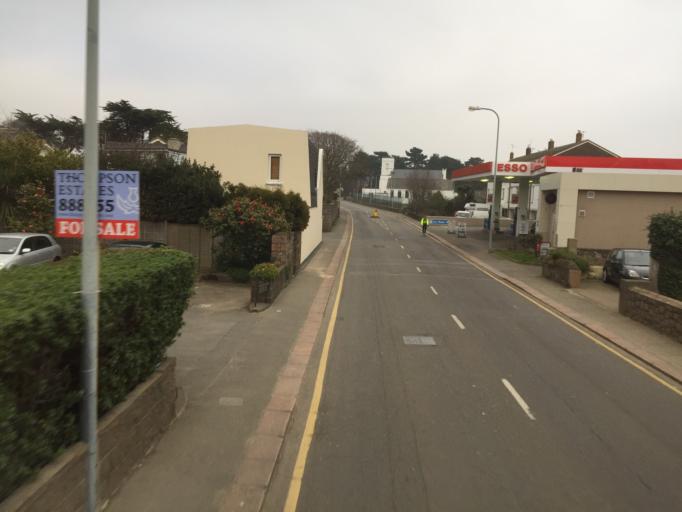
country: JE
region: St Helier
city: Saint Helier
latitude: 49.1983
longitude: -2.1456
